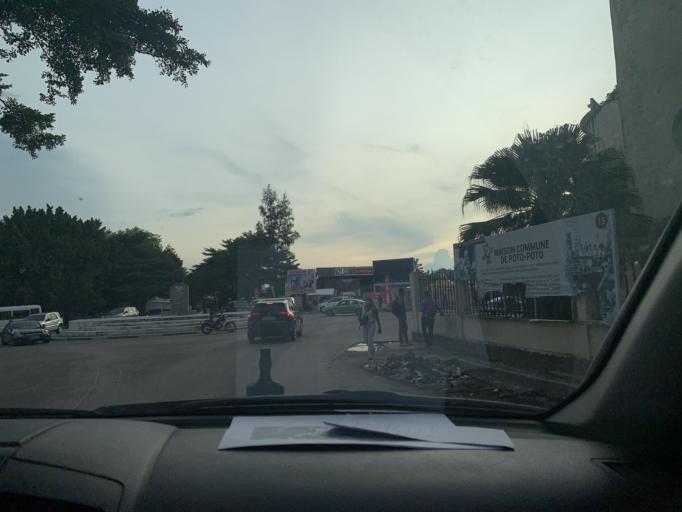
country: CG
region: Brazzaville
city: Brazzaville
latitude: -4.2667
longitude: 15.2849
